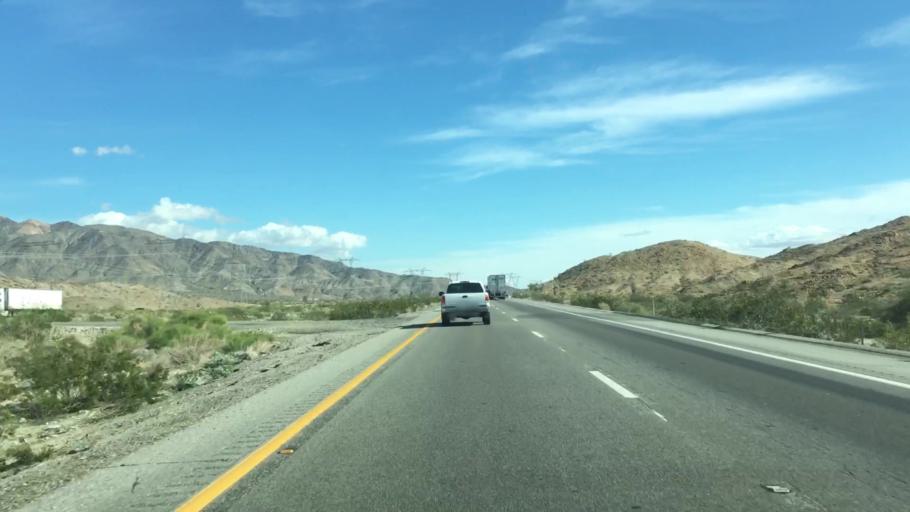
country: US
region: California
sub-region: Riverside County
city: Mecca
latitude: 33.6798
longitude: -115.9782
